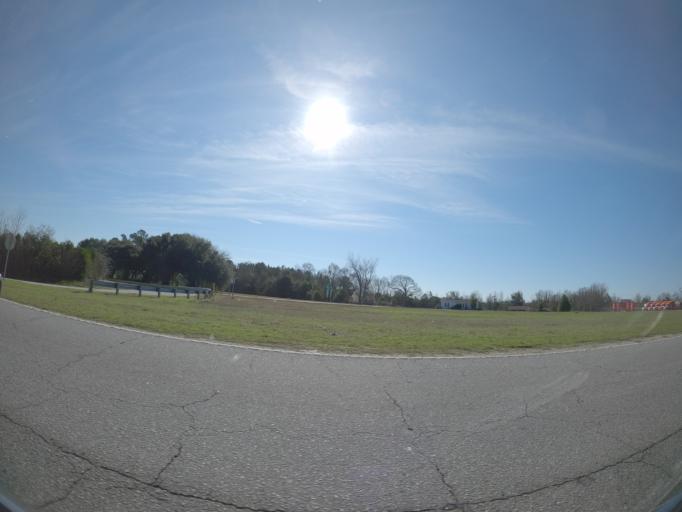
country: US
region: South Carolina
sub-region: Aiken County
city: Clearwater
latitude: 33.4891
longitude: -81.9216
